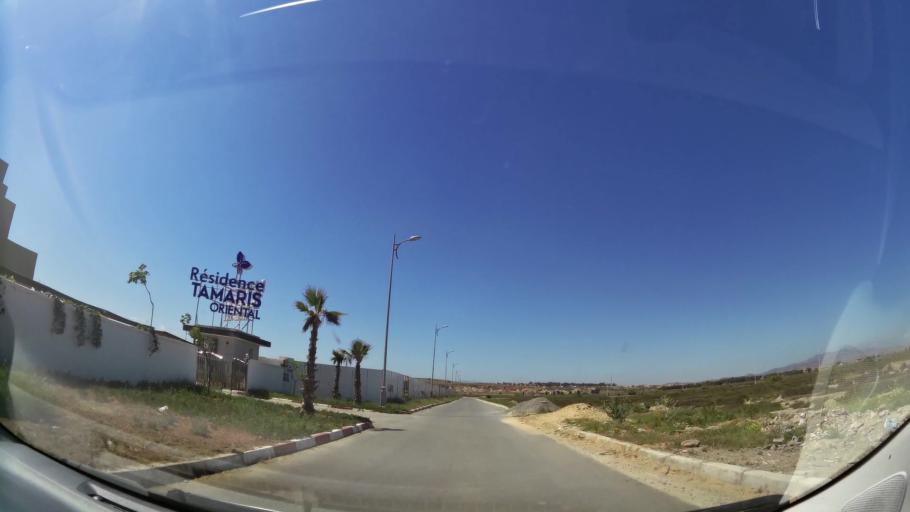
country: MA
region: Oriental
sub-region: Berkane-Taourirt
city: Madagh
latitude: 35.1076
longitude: -2.3169
